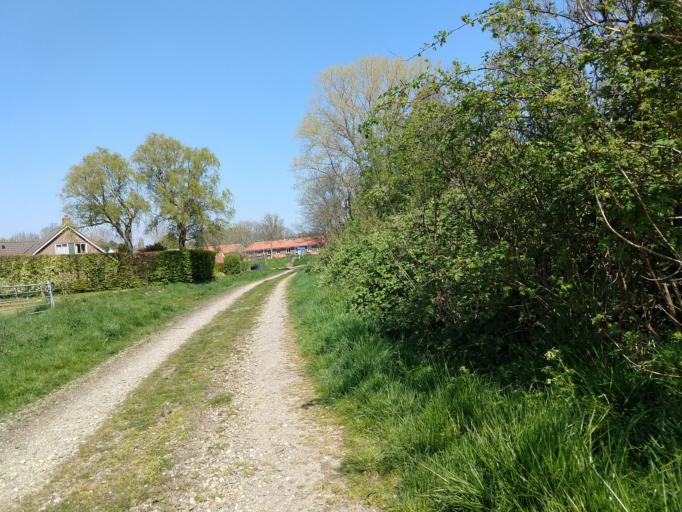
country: NL
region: Zeeland
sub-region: Gemeente Goes
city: Goes
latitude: 51.4902
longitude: 3.8189
